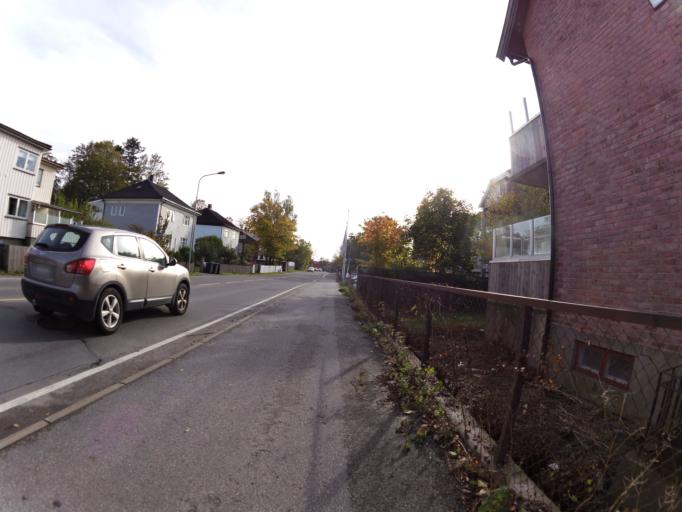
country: NO
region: Ostfold
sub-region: Fredrikstad
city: Fredrikstad
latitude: 59.2235
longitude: 10.9302
